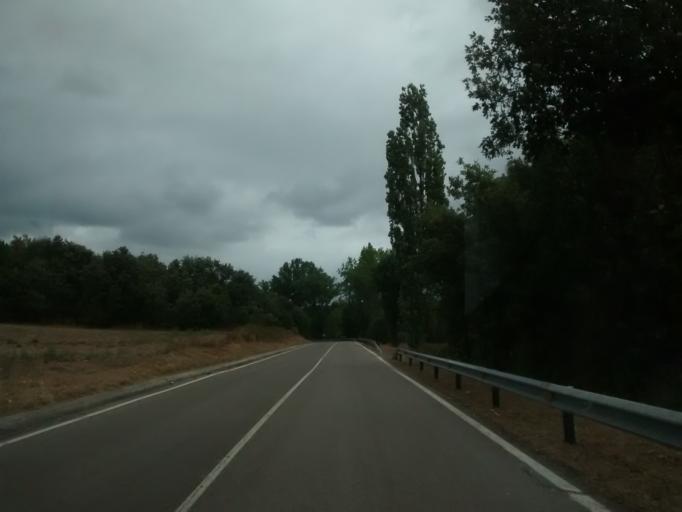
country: ES
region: Castille and Leon
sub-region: Provincia de Palencia
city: Berzosilla
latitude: 42.7880
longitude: -3.9915
